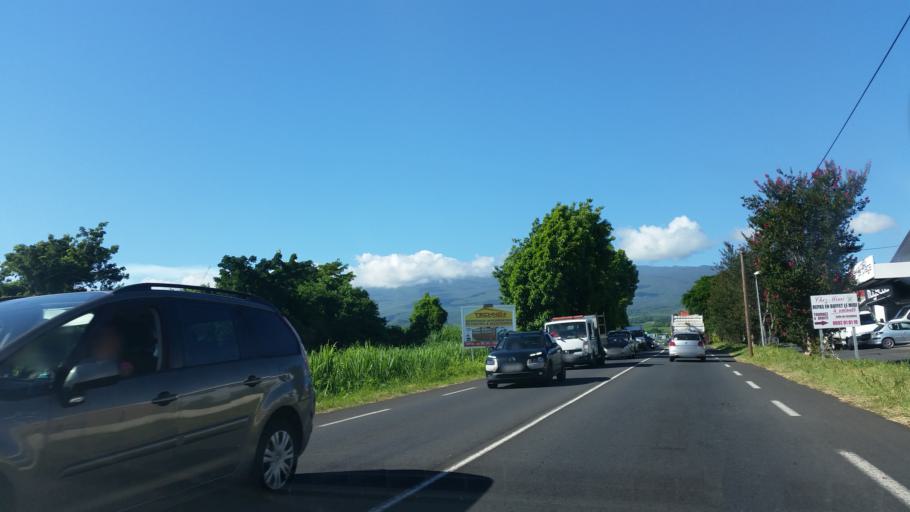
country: RE
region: Reunion
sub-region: Reunion
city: Saint-Benoit
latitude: -21.0537
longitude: 55.7140
